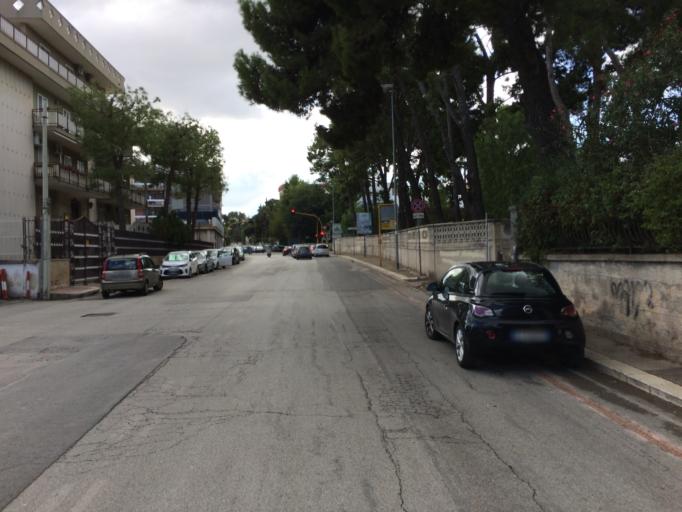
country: IT
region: Apulia
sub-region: Provincia di Bari
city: Bari
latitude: 41.1023
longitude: 16.8794
